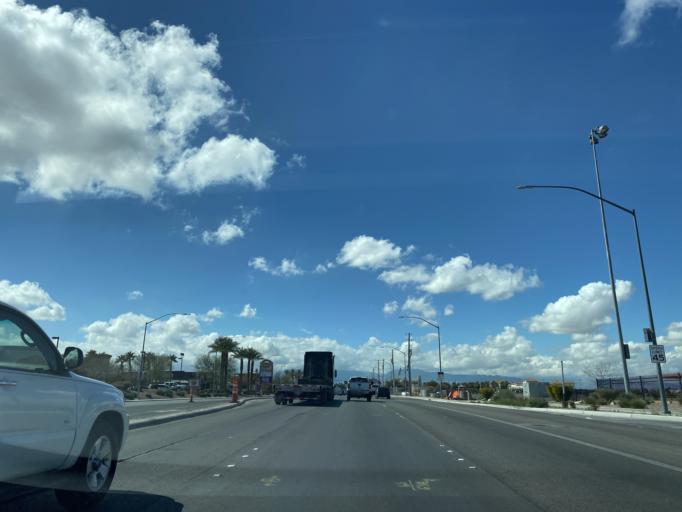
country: US
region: Nevada
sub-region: Clark County
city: North Las Vegas
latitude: 36.2395
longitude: -115.1536
